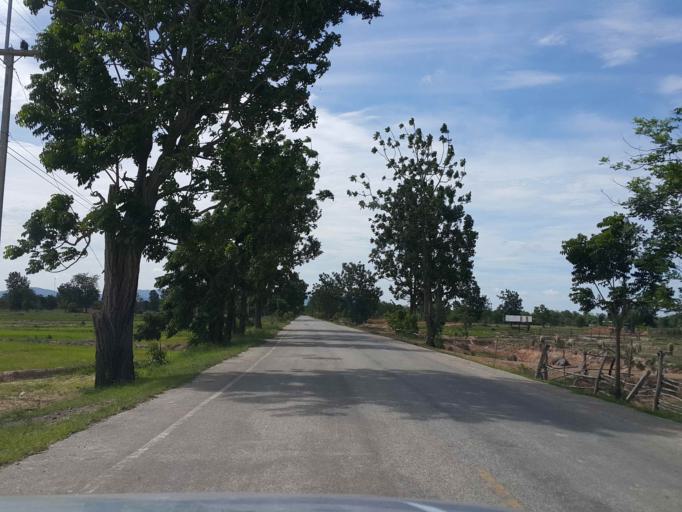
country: TH
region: Sukhothai
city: Ban Dan Lan Hoi
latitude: 17.1301
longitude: 99.5284
